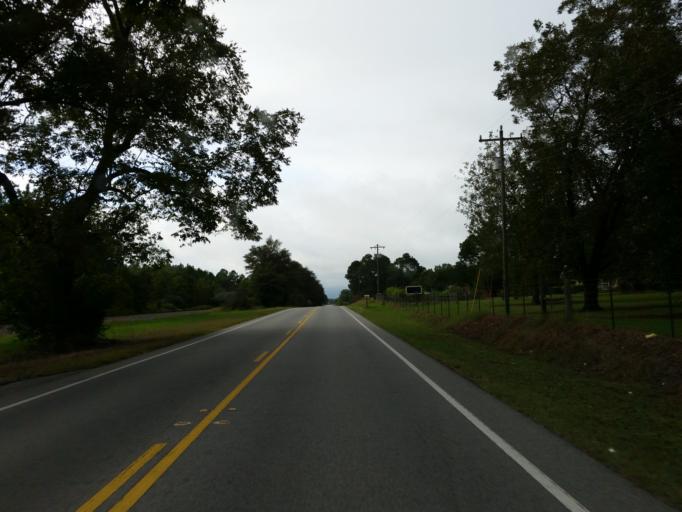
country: US
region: Georgia
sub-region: Tift County
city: Tifton
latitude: 31.5723
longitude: -83.5670
